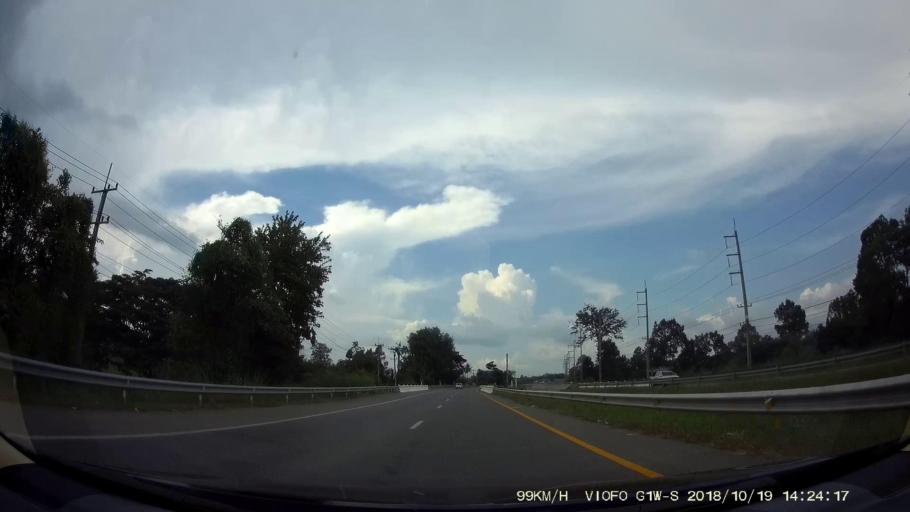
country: TH
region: Chaiyaphum
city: Kaeng Khro
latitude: 16.0790
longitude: 102.2743
